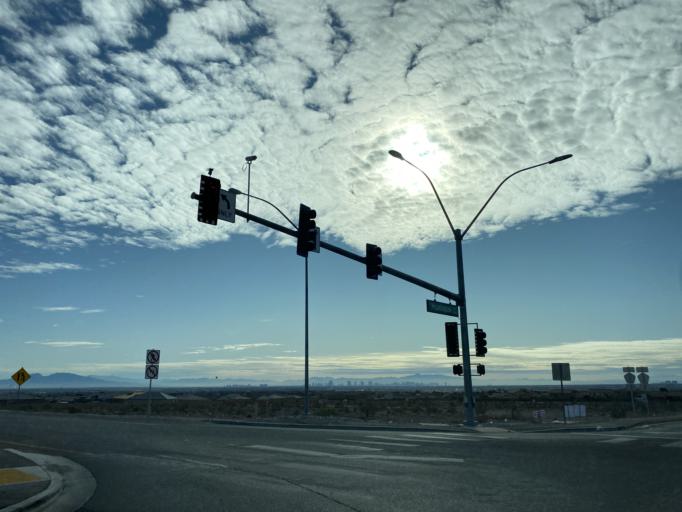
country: US
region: Nevada
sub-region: Clark County
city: Summerlin South
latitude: 36.2806
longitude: -115.3150
